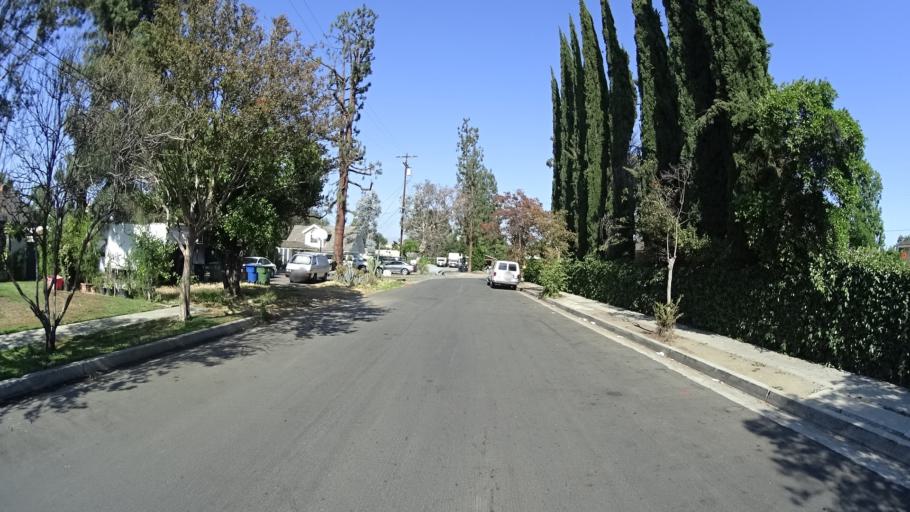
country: US
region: California
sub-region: Los Angeles County
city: Van Nuys
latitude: 34.1929
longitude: -118.4287
